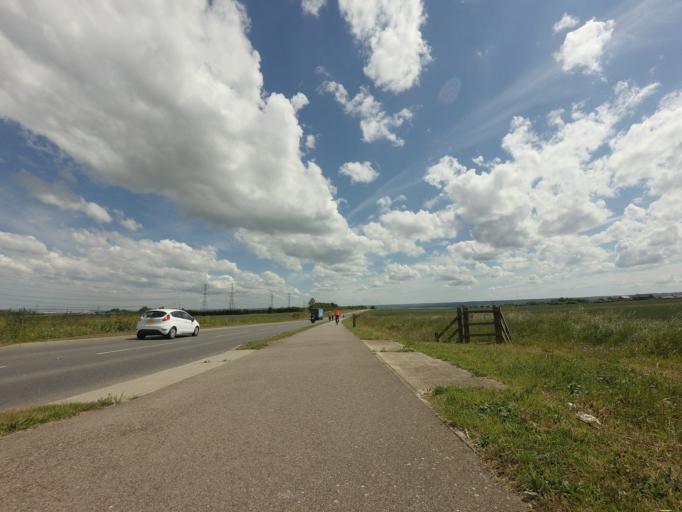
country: GB
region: England
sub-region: Kent
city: Hoo
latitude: 51.4340
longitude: 0.5700
